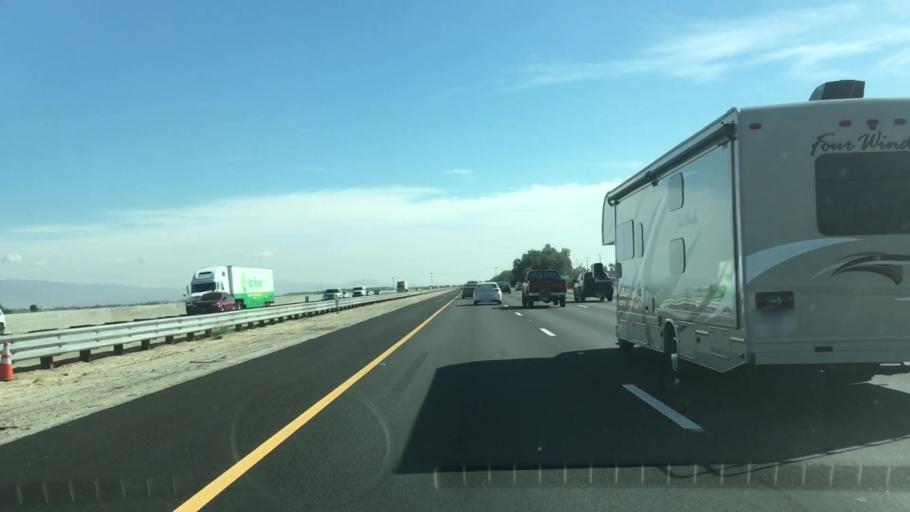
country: US
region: California
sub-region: Riverside County
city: Indian Wells
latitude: 33.7768
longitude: -116.3392
